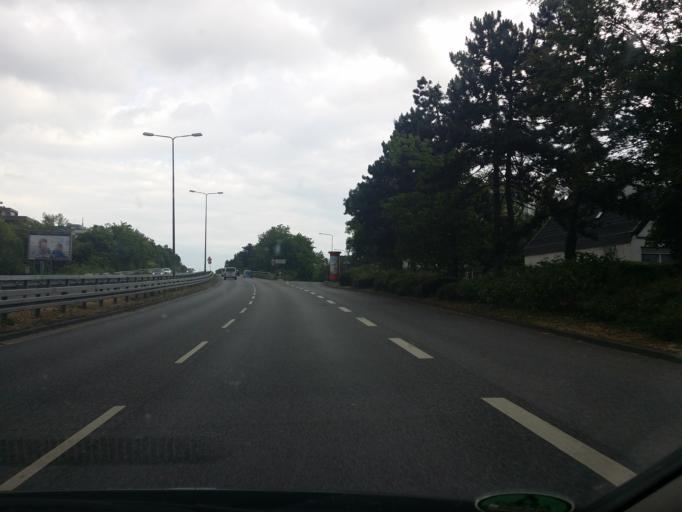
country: DE
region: Hesse
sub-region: Regierungsbezirk Darmstadt
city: Wiesbaden
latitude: 50.0689
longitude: 8.2619
